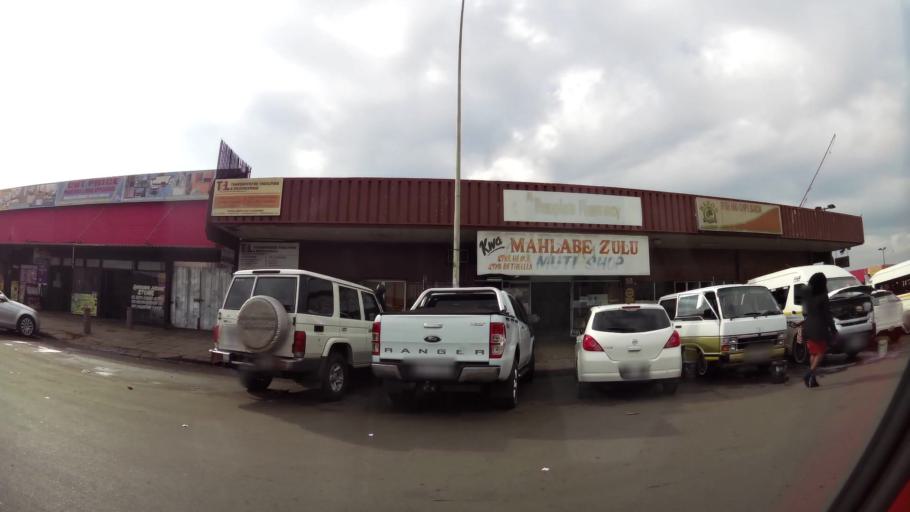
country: ZA
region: Gauteng
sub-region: Sedibeng District Municipality
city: Vanderbijlpark
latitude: -26.6967
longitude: 27.8388
